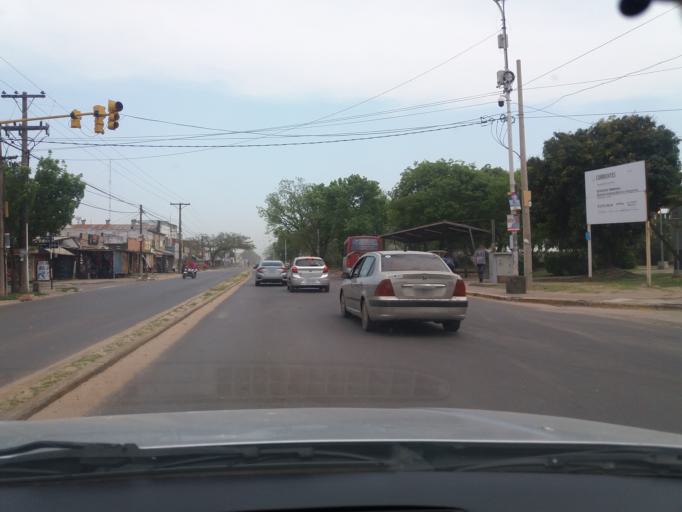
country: AR
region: Corrientes
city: Corrientes
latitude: -27.4984
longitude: -58.8150
